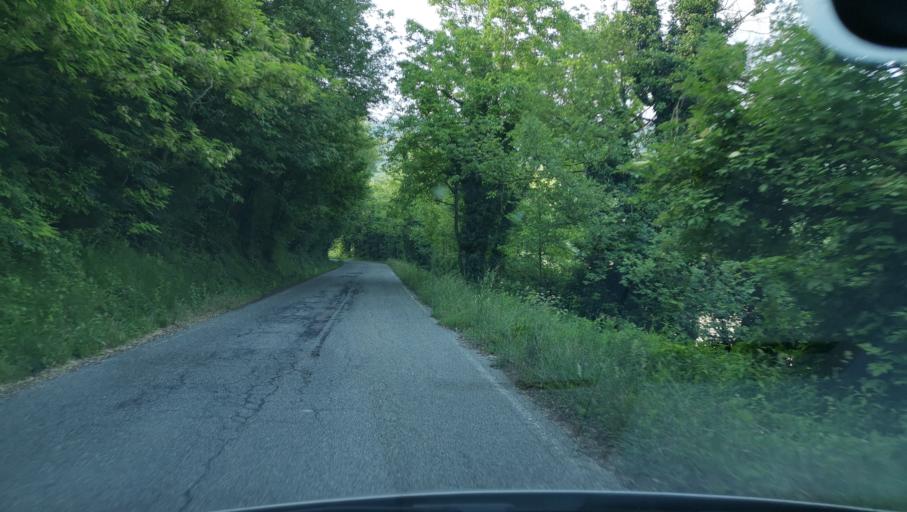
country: IT
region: Piedmont
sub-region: Provincia di Alessandria
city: Odalengo Piccolo
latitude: 45.0796
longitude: 8.1936
